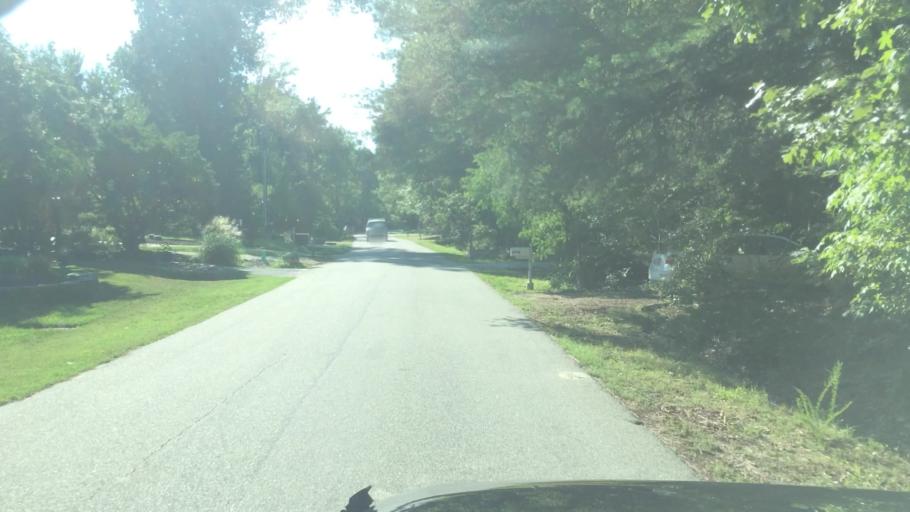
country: US
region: Virginia
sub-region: James City County
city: Williamsburg
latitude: 37.2365
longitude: -76.8013
